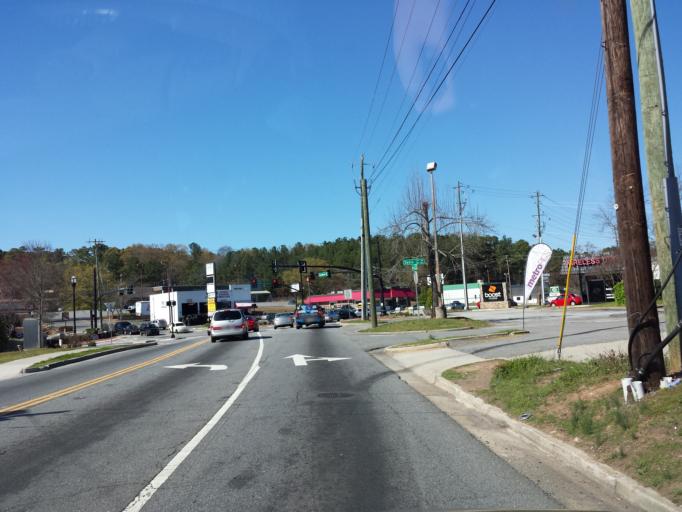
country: US
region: Georgia
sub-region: Cobb County
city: Marietta
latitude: 33.9353
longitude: -84.5559
